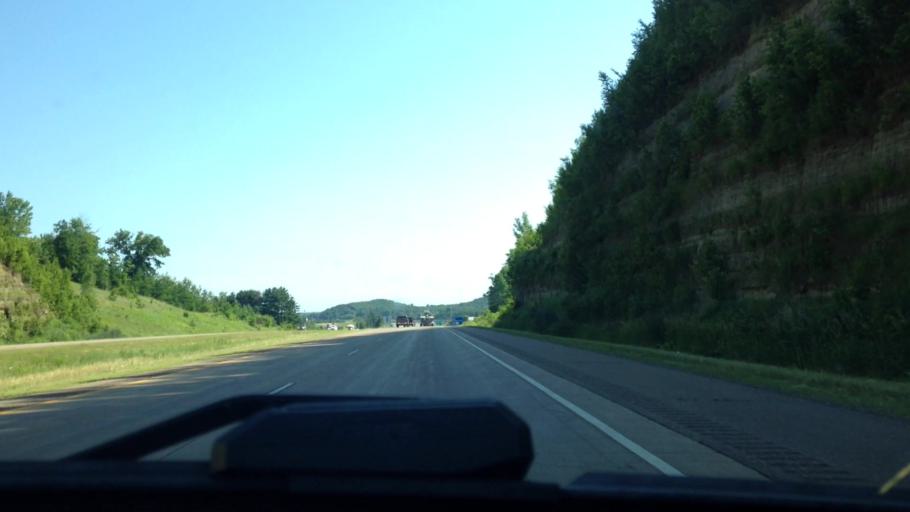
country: US
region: Wisconsin
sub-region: Chippewa County
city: Lake Hallie
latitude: 44.8525
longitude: -91.4351
